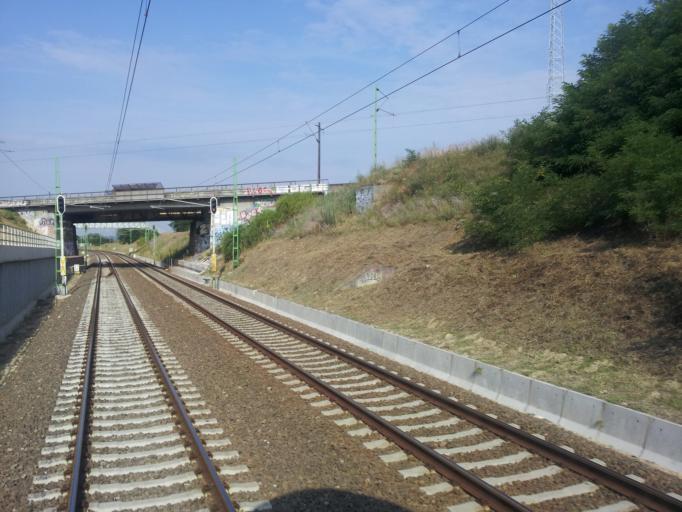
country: HU
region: Pest
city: Erd
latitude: 47.3764
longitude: 18.9015
